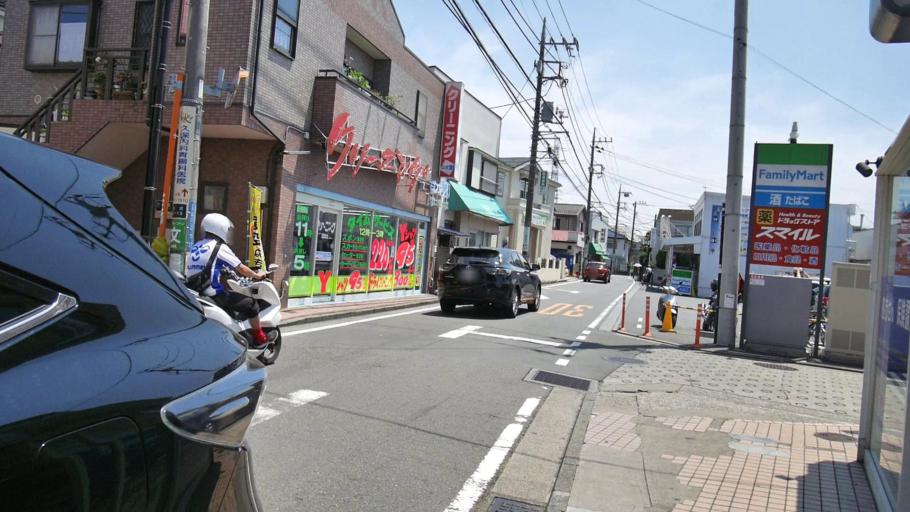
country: JP
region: Kanagawa
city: Fujisawa
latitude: 35.4030
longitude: 139.5175
